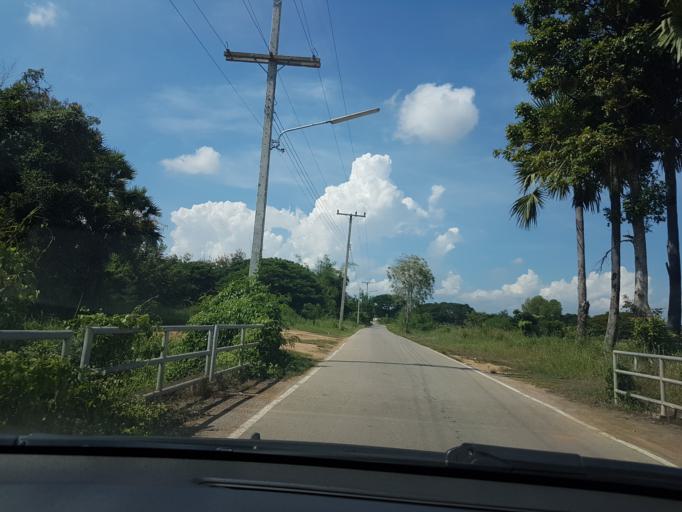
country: TH
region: Lampang
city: Ko Kha
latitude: 18.2107
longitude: 99.3949
